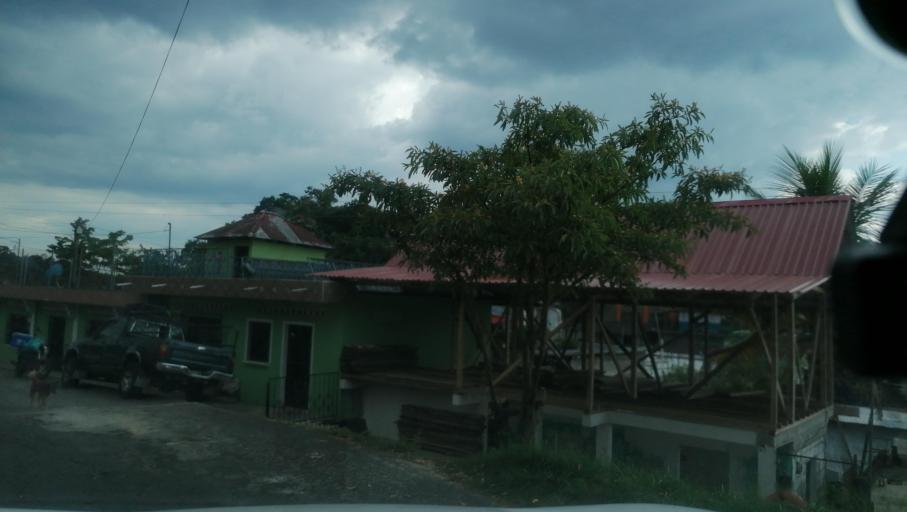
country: MX
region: Chiapas
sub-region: Cacahoatan
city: Benito Juarez
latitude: 15.0741
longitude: -92.1985
